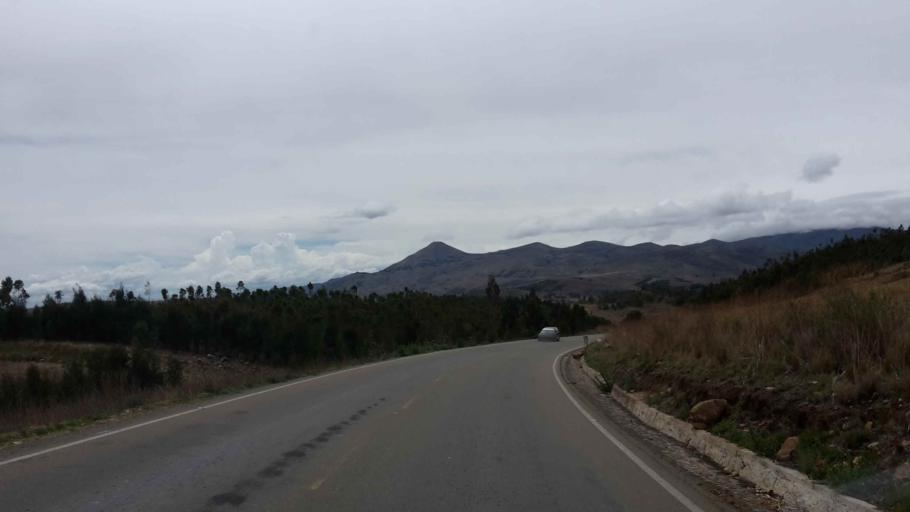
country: BO
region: Cochabamba
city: Arani
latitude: -17.4622
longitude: -65.7007
